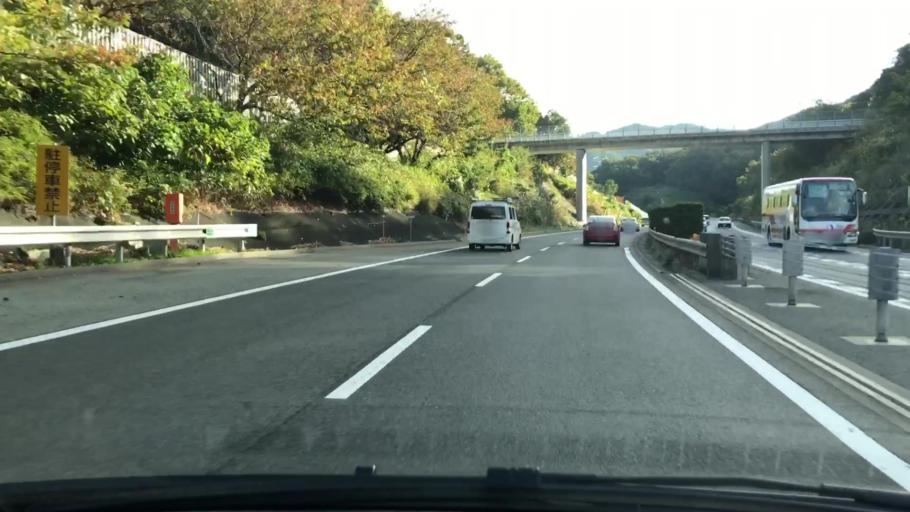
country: JP
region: Hyogo
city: Kobe
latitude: 34.7631
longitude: 135.1893
